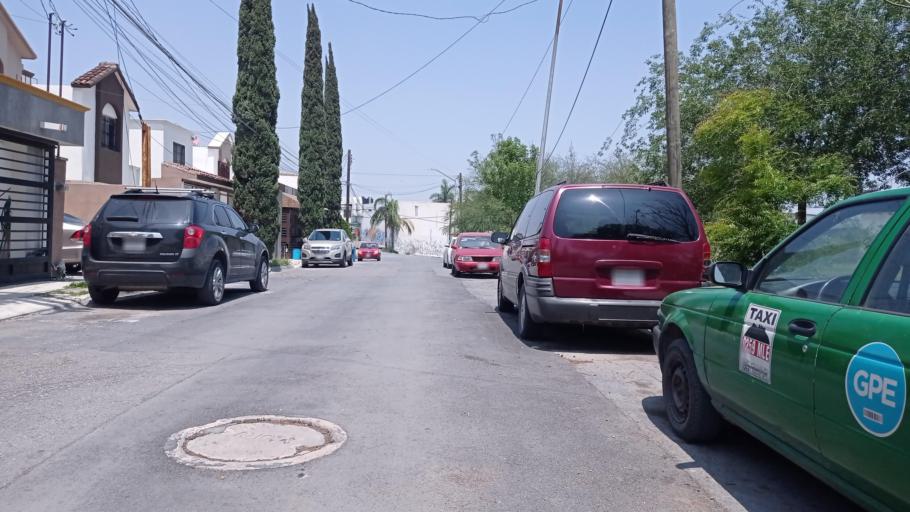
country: MX
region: Nuevo Leon
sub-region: Juarez
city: Jardines de la Silla (Jardines)
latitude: 25.6554
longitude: -100.1899
